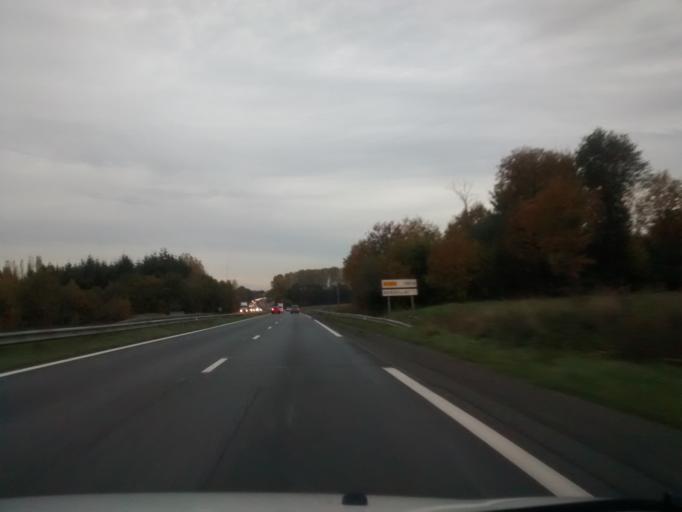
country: FR
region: Brittany
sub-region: Departement d'Ille-et-Vilaine
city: Quedillac
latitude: 48.2438
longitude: -2.1304
